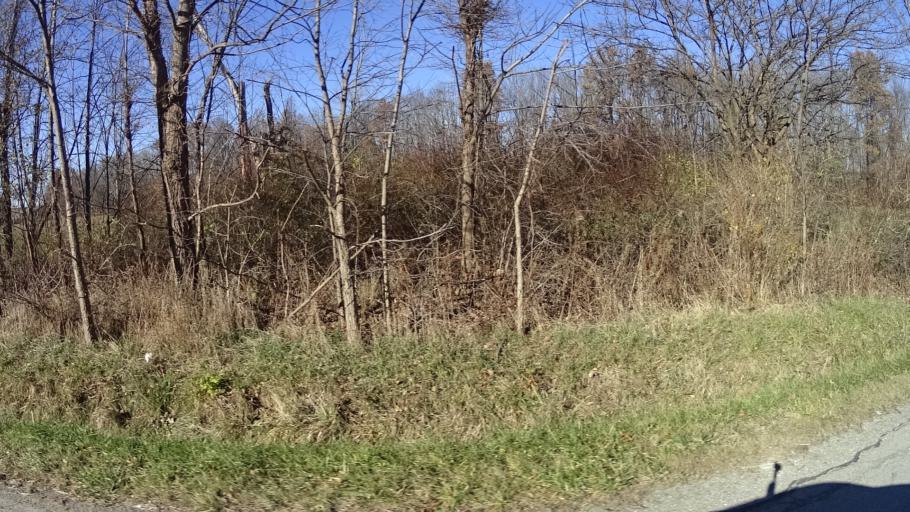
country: US
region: Ohio
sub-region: Lorain County
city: Oberlin
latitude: 41.3049
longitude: -82.1530
